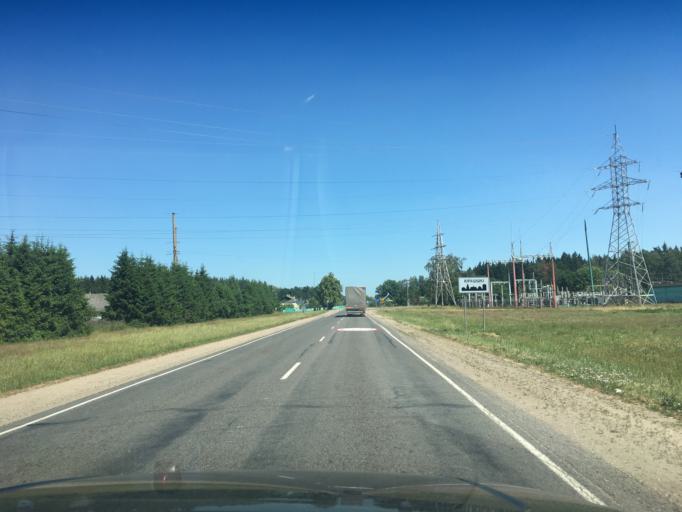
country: BY
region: Grodnenskaya
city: Iwye
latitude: 54.0244
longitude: 25.9177
